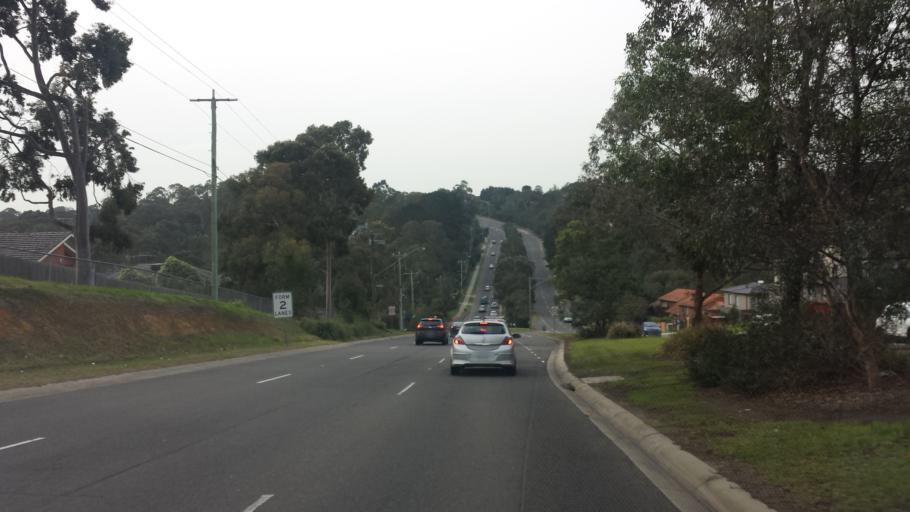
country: AU
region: Victoria
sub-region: Manningham
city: Templestowe Lower
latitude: -37.7691
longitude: 145.1301
